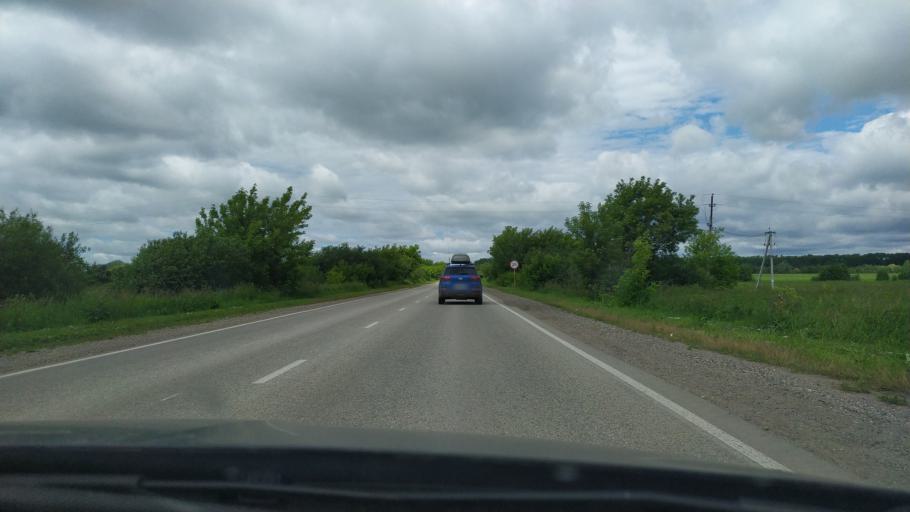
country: RU
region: Perm
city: Kondratovo
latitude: 57.9300
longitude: 56.0997
